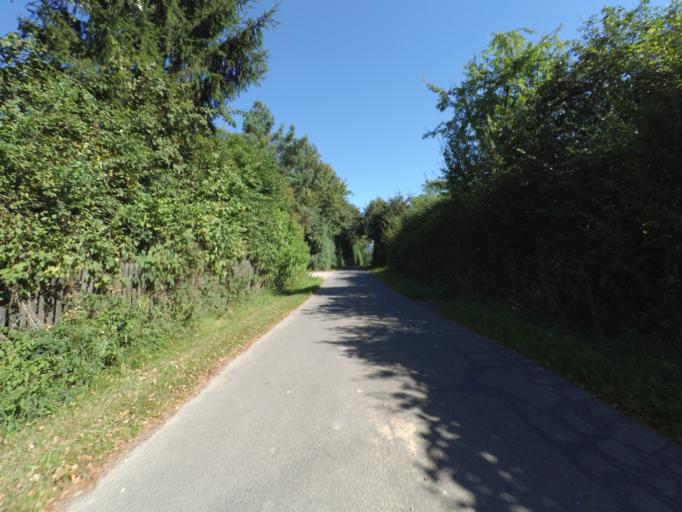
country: DE
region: Rheinland-Pfalz
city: Gefell
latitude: 50.2193
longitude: 6.9192
